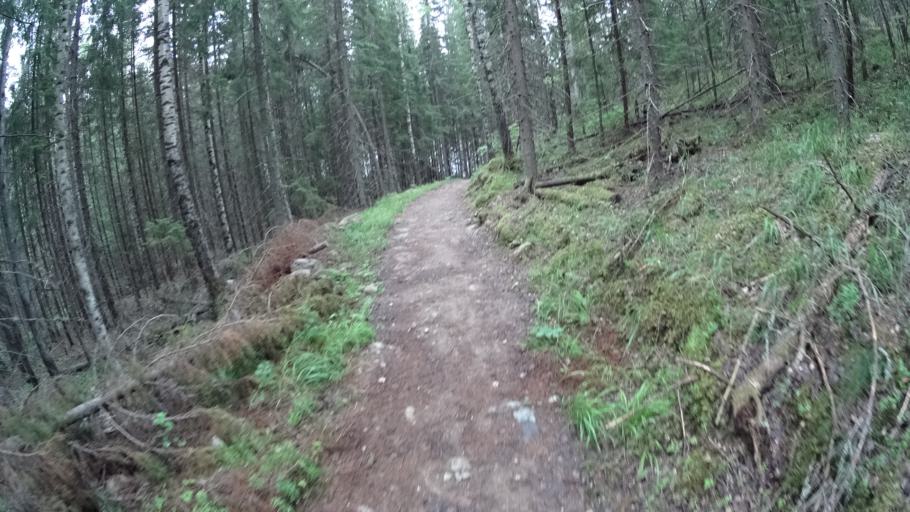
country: FI
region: Southern Savonia
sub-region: Mikkeli
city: Maentyharju
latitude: 61.1802
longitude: 26.8969
